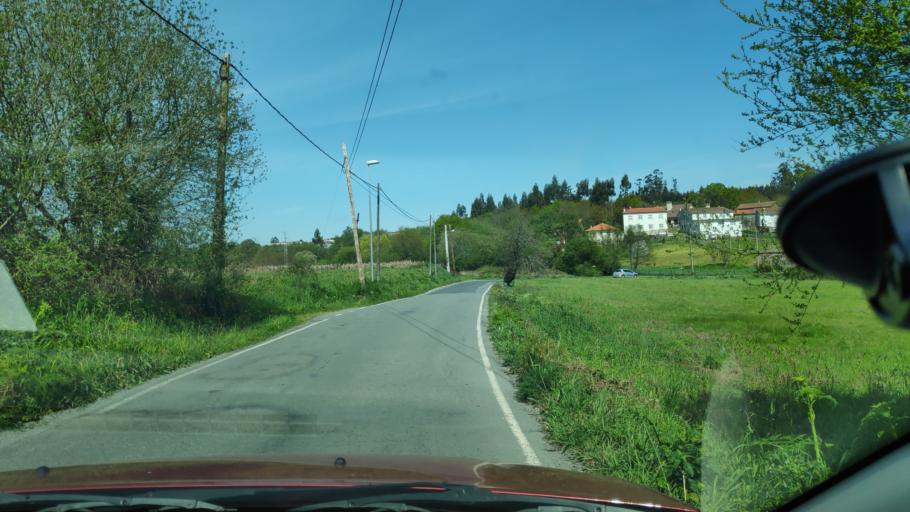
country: ES
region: Galicia
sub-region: Provincia da Coruna
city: Santiago de Compostela
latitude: 42.8937
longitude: -8.5251
